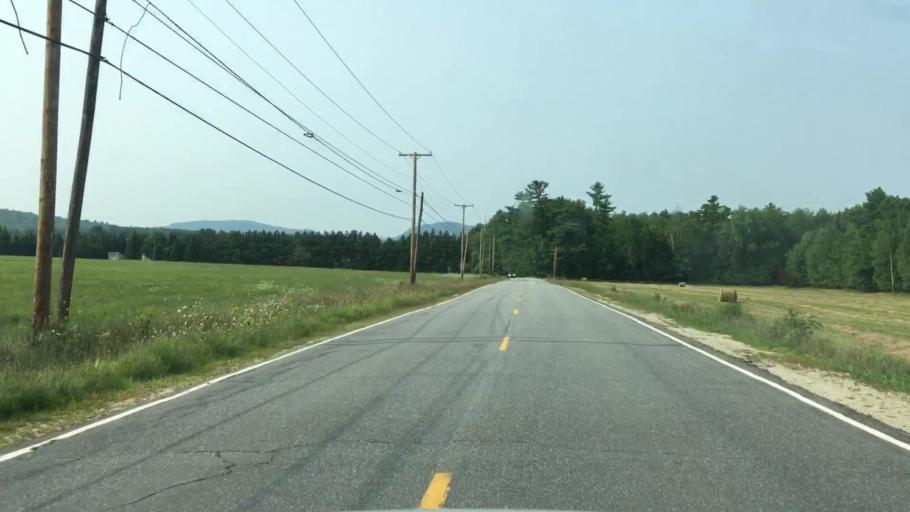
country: US
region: Maine
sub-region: Oxford County
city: Norway
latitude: 44.2275
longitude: -70.5948
